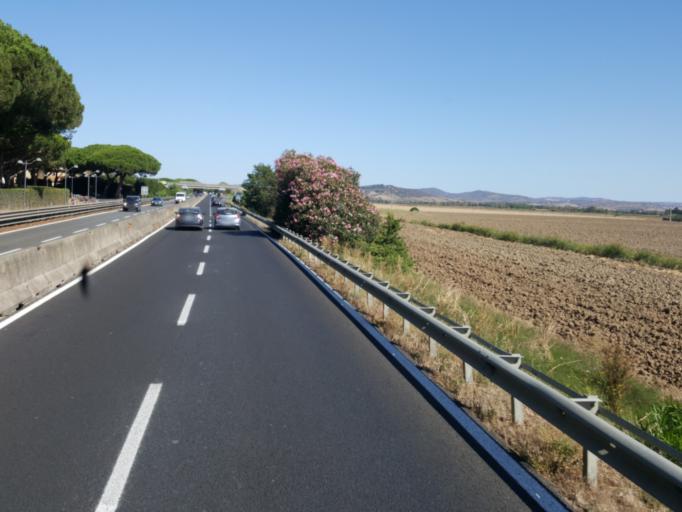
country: IT
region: Tuscany
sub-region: Provincia di Grosseto
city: Albinia
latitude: 42.5198
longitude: 11.1928
